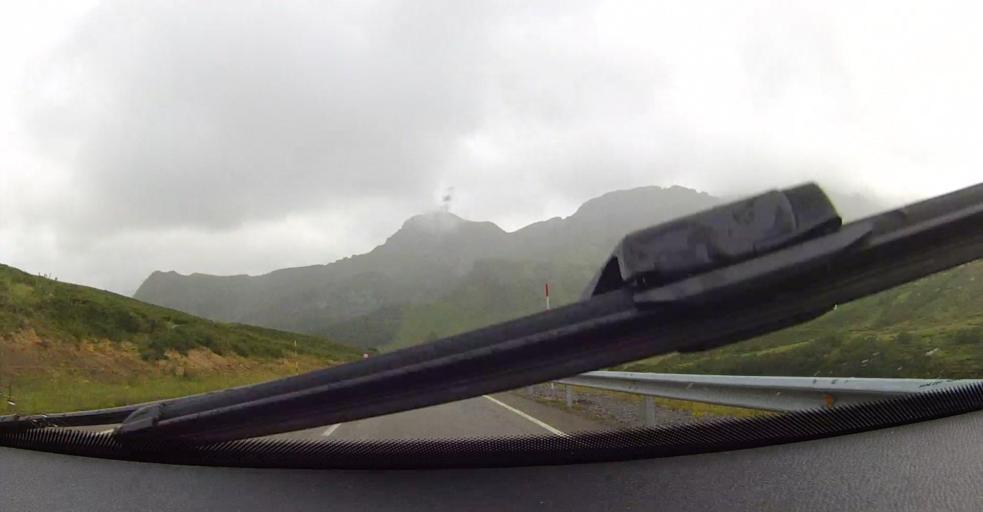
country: ES
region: Castille and Leon
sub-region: Provincia de Leon
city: Marana
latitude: 43.0792
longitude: -5.2138
